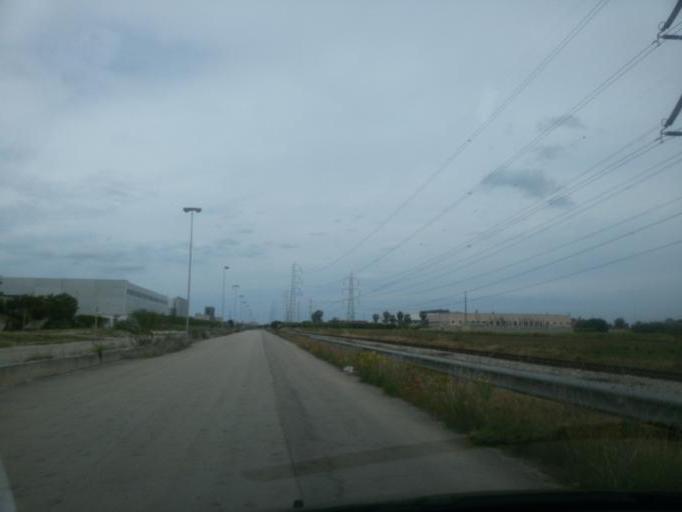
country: IT
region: Apulia
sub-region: Provincia di Brindisi
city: Materdomini
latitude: 40.6287
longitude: 17.9805
